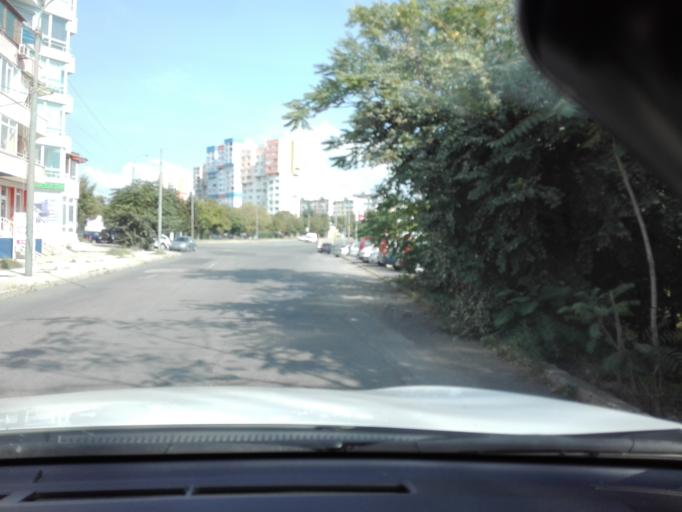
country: BG
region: Burgas
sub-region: Obshtina Burgas
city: Burgas
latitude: 42.4591
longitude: 27.4234
